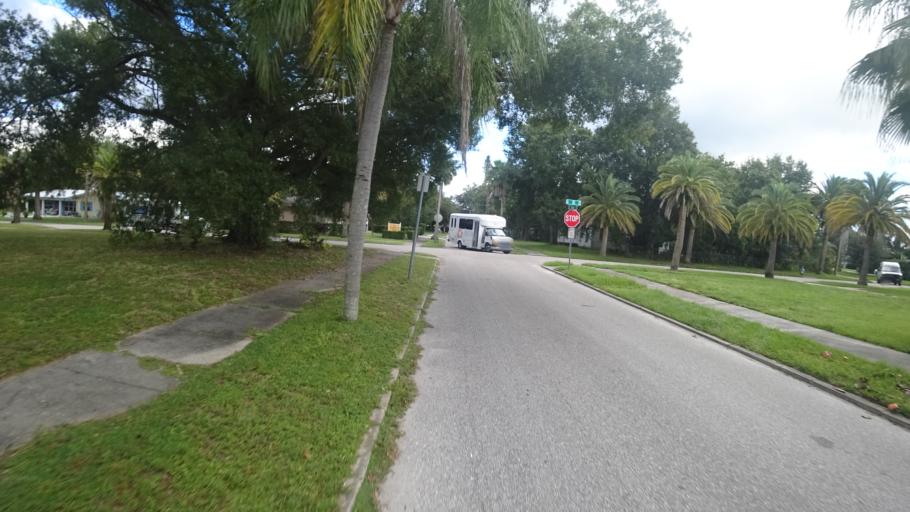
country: US
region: Florida
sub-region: Manatee County
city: Bradenton
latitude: 27.4975
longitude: -82.5598
